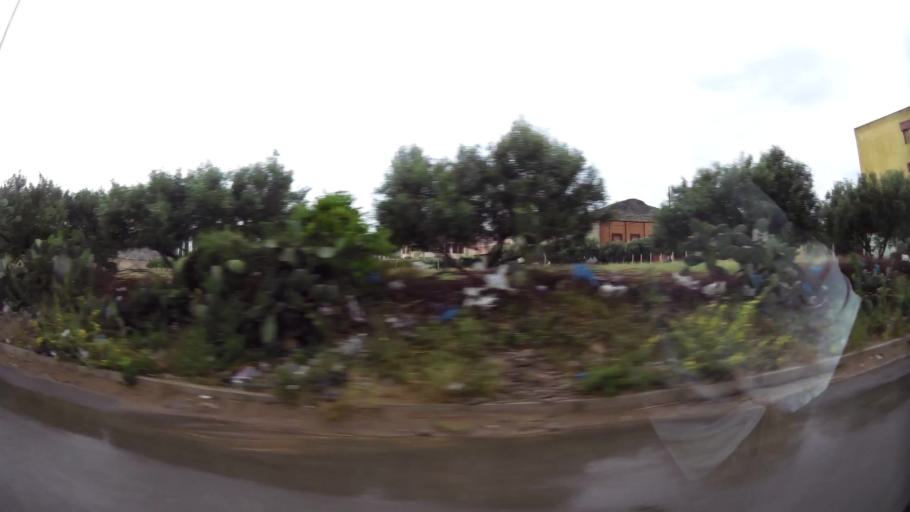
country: MA
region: Oriental
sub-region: Nador
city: Nador
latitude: 35.1498
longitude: -2.9927
